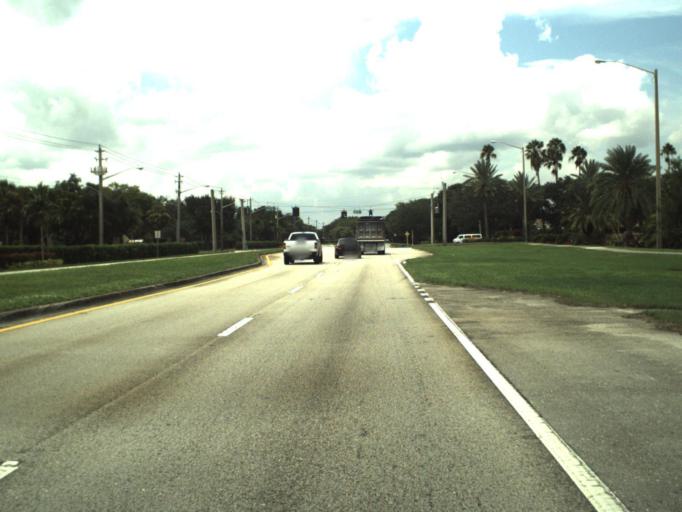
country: US
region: Florida
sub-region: Broward County
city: Cooper City
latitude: 26.0299
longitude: -80.2871
